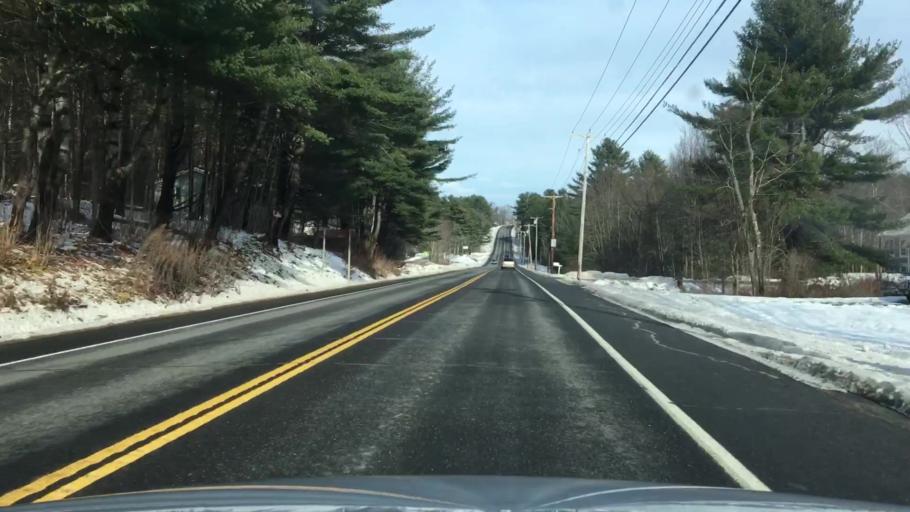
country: US
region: Maine
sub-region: Androscoggin County
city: Greene
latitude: 44.1675
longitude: -70.1781
